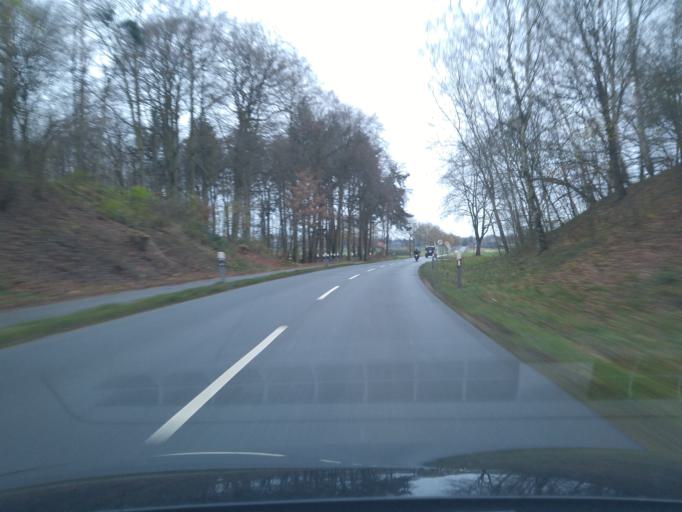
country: DE
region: Lower Saxony
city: Scharnebeck
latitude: 53.2776
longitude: 10.5030
